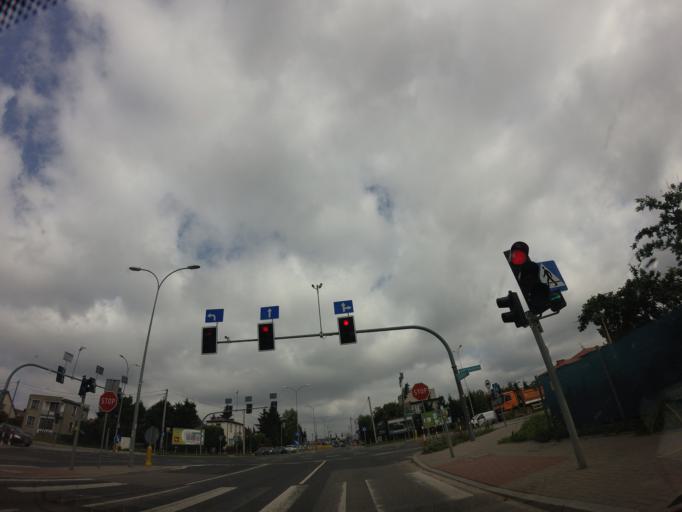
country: PL
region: Podlasie
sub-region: Bialystok
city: Bialystok
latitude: 53.1140
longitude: 23.1788
